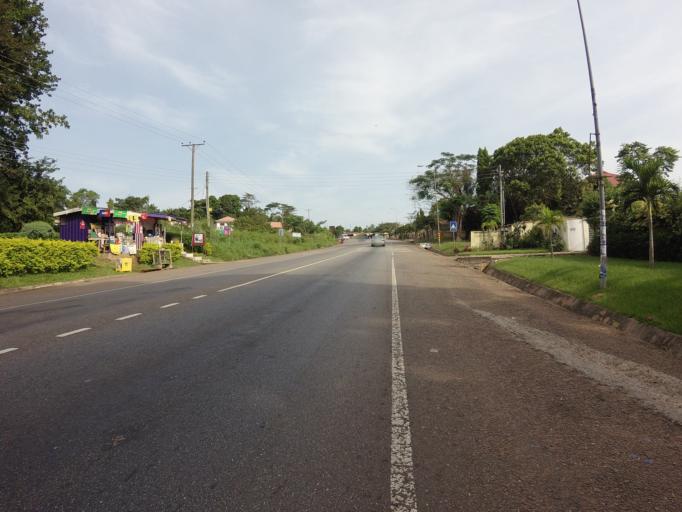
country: GH
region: Eastern
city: Aburi
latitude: 5.8105
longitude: -0.1848
